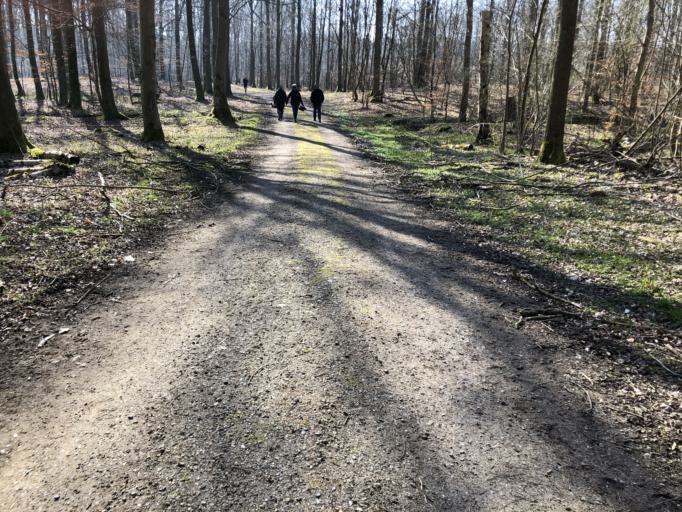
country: DK
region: Capital Region
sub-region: Allerod Kommune
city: Blovstrod
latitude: 55.8998
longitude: 12.3899
